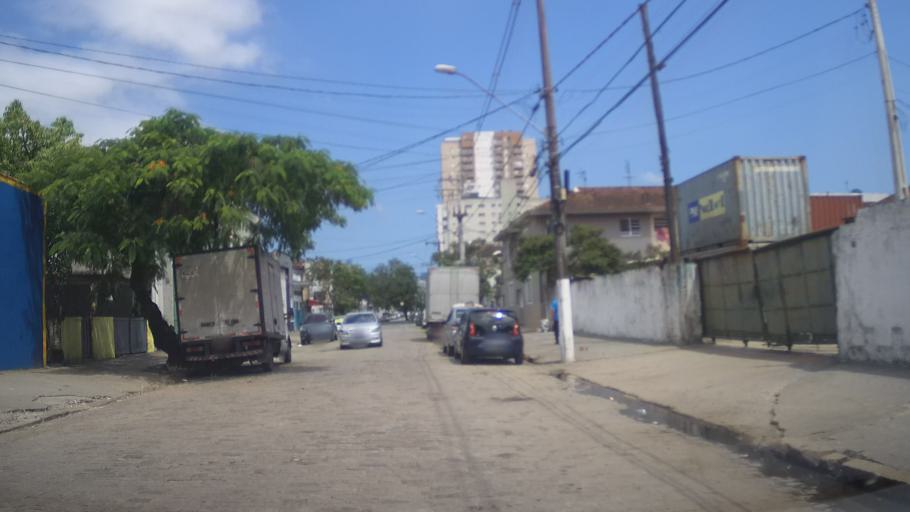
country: BR
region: Sao Paulo
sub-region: Santos
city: Santos
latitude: -23.9594
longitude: -46.3112
